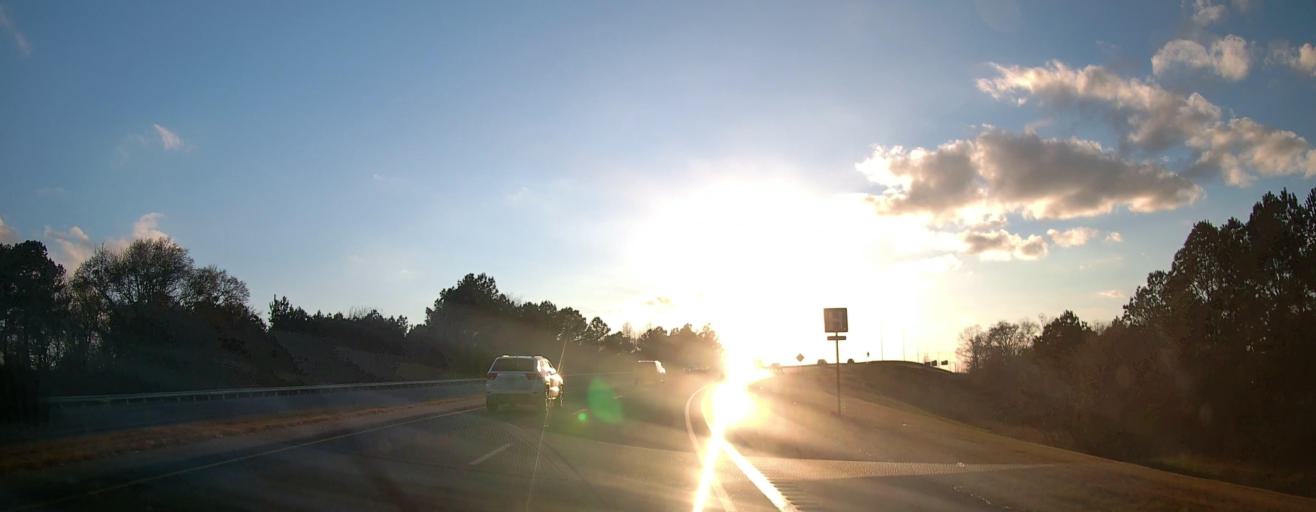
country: US
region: Alabama
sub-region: Etowah County
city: Gadsden
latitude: 33.9955
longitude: -85.9959
